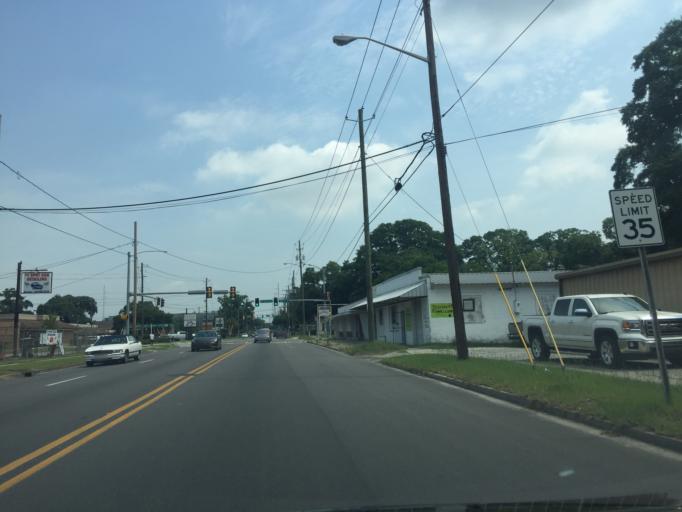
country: US
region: Georgia
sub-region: Chatham County
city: Savannah
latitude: 32.0439
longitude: -81.1098
